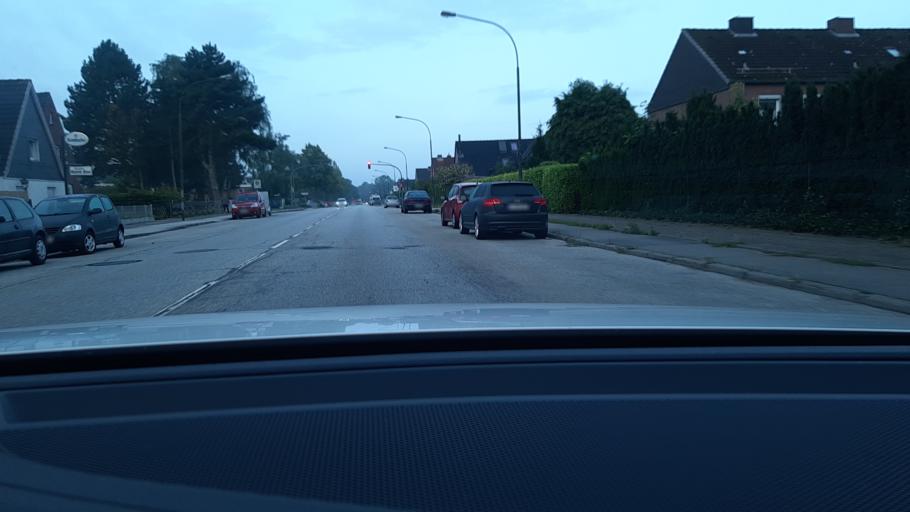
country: DE
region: Schleswig-Holstein
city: Stockelsdorf
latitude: 53.8596
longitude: 10.6462
